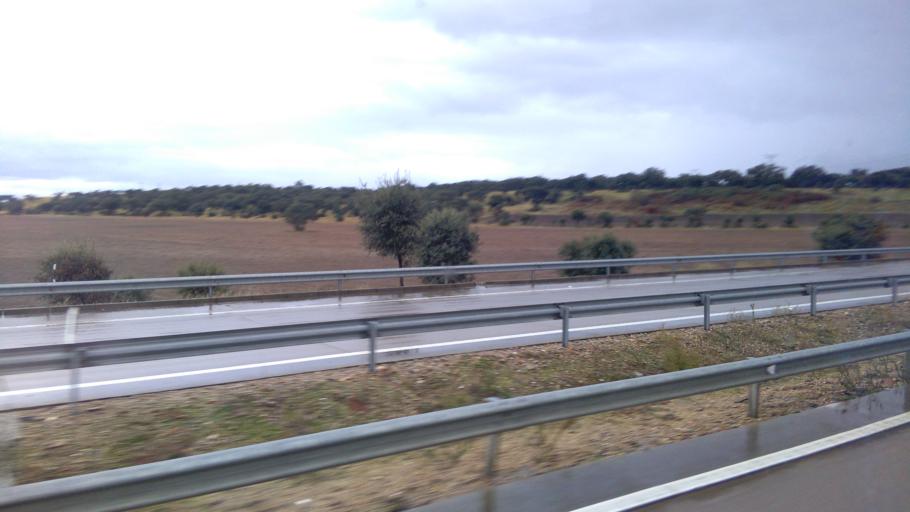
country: ES
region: Castille-La Mancha
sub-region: Province of Toledo
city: Cervera de los Montes
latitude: 40.0065
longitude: -4.7713
